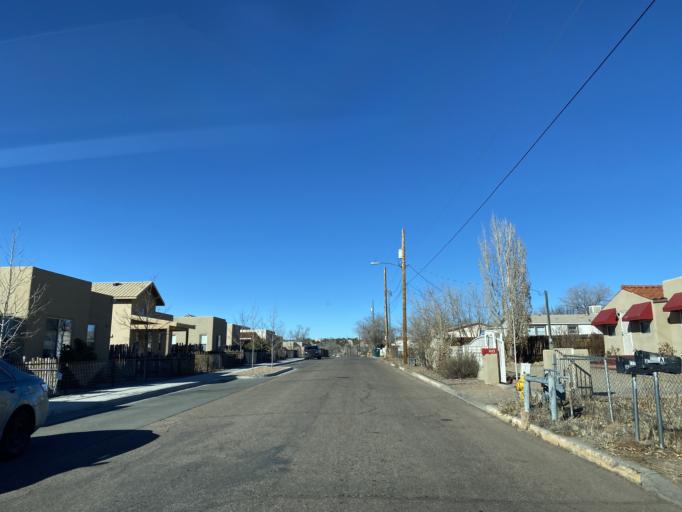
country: US
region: New Mexico
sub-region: Santa Fe County
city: Agua Fria
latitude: 35.6647
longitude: -105.9895
